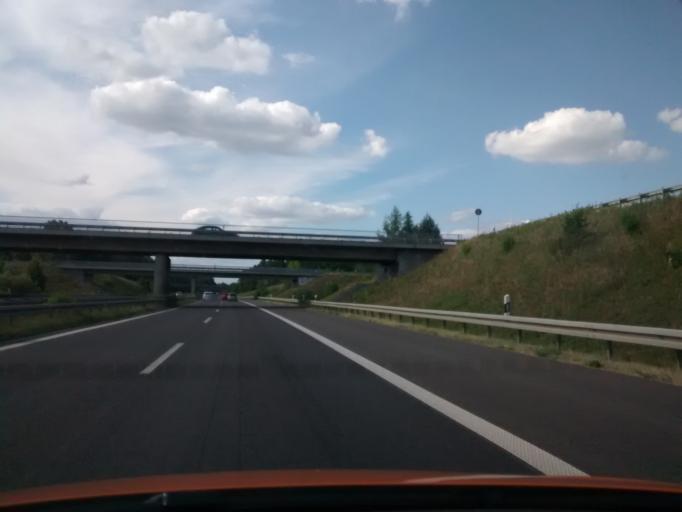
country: DE
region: Brandenburg
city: Grossbeeren
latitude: 52.3277
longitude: 13.2861
